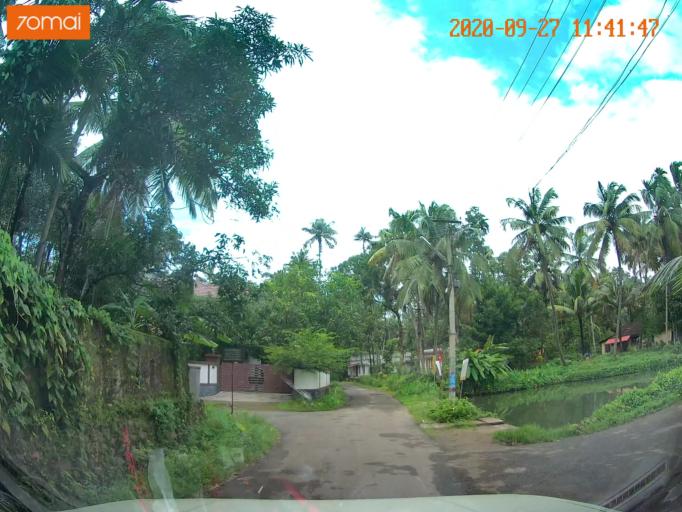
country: IN
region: Kerala
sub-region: Thrissur District
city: Thanniyam
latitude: 10.4714
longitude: 76.1144
